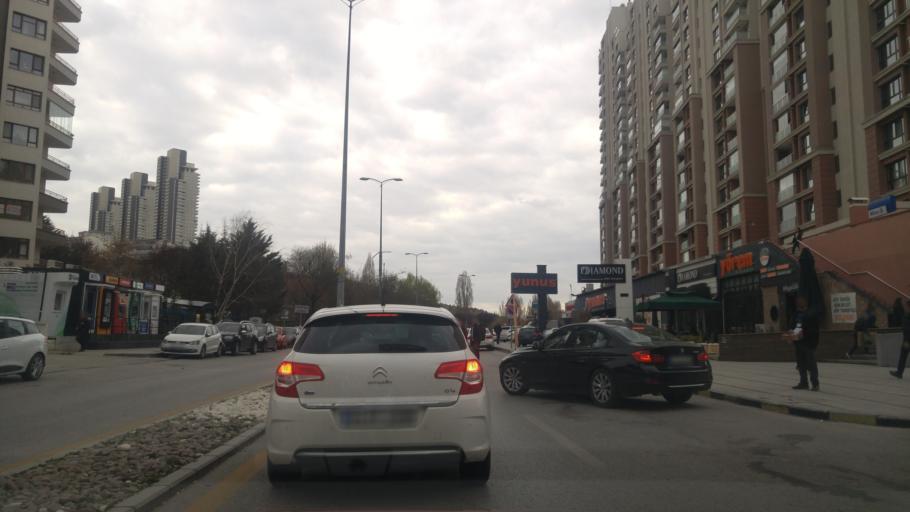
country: TR
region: Ankara
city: Batikent
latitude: 39.8986
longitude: 32.6919
